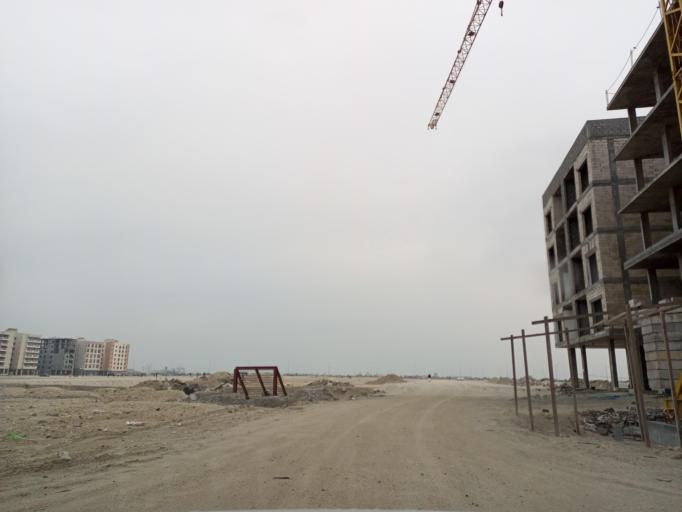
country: BH
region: Muharraq
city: Al Hadd
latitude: 26.2306
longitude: 50.6423
